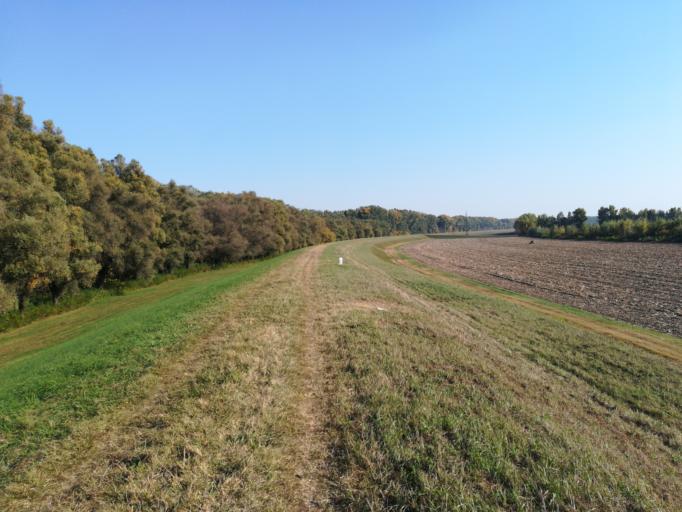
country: HU
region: Bacs-Kiskun
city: Tiszakecske
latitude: 46.9376
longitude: 20.1395
